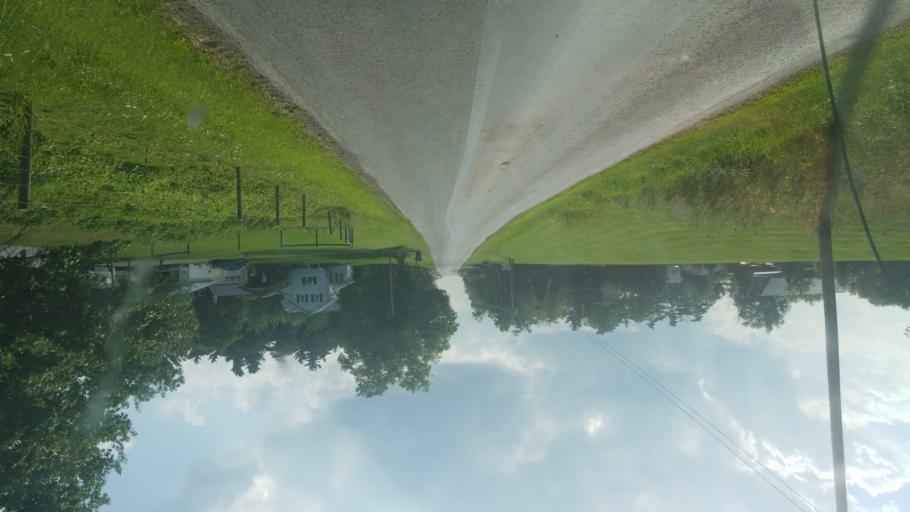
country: US
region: Ohio
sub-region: Wayne County
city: West Salem
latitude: 40.9524
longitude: -82.0685
